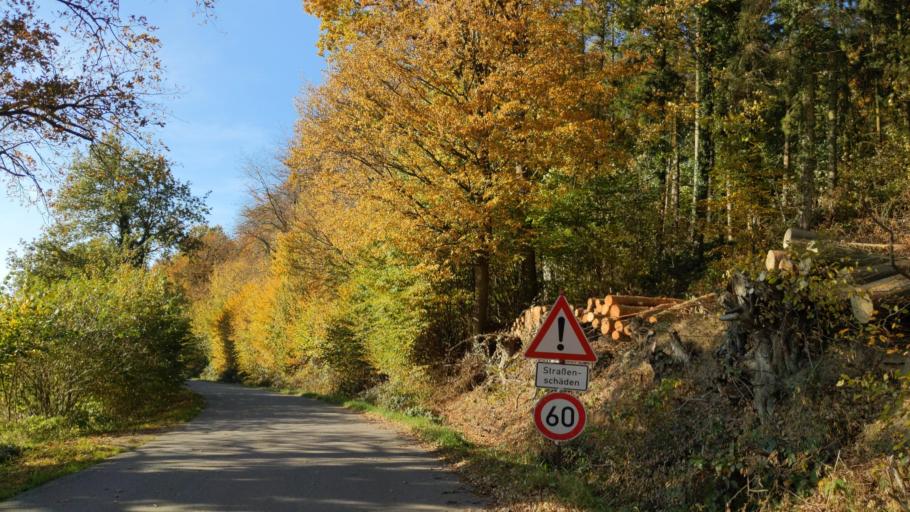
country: DE
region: Schleswig-Holstein
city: Kasseedorf
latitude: 54.1380
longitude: 10.7156
